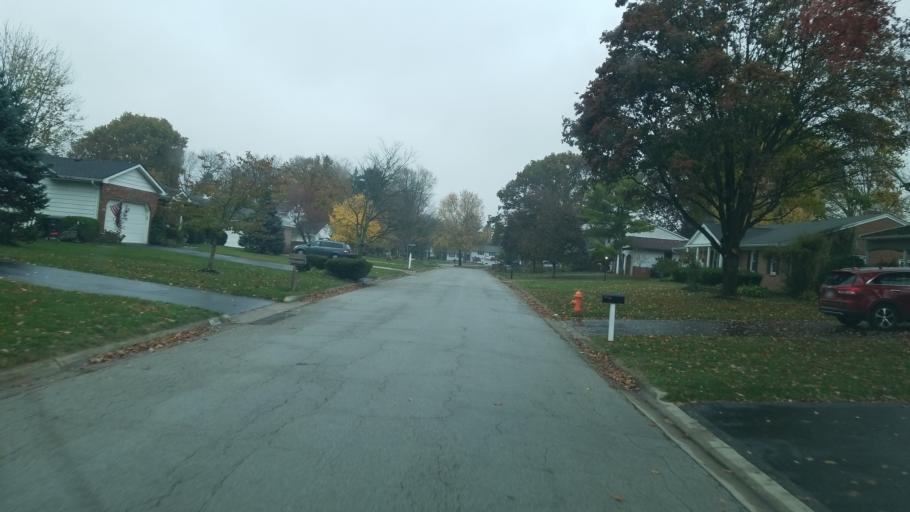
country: US
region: Ohio
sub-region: Franklin County
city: Worthington
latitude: 40.0810
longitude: -83.0465
